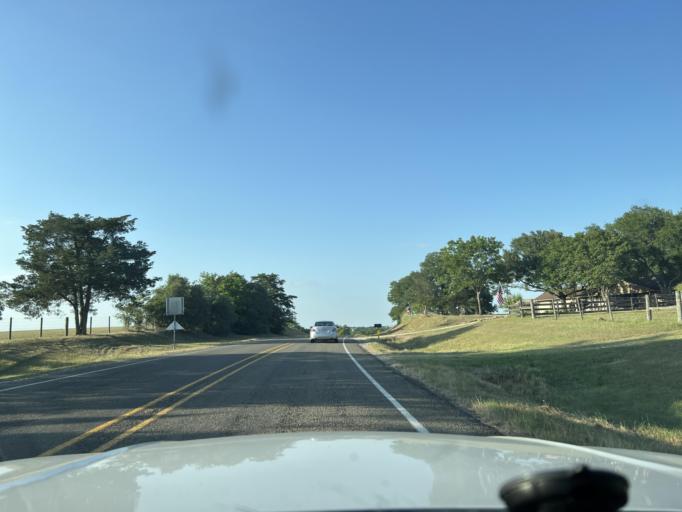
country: US
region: Texas
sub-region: Washington County
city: Brenham
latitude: 30.2093
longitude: -96.3929
